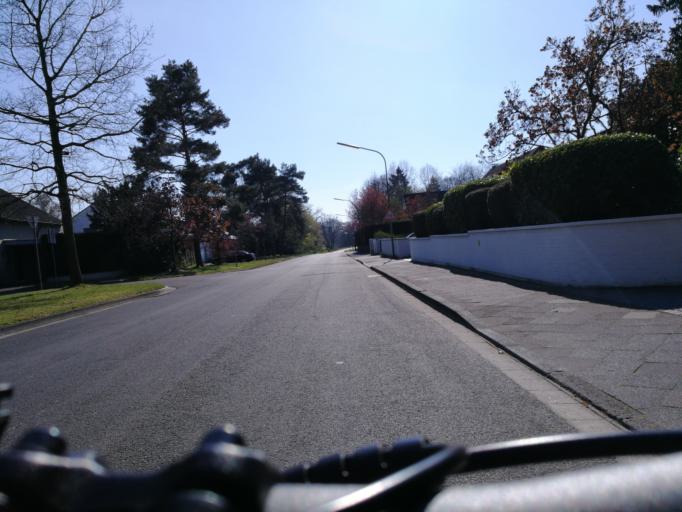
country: DE
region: North Rhine-Westphalia
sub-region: Regierungsbezirk Dusseldorf
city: Neuss
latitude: 51.1802
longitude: 6.7252
